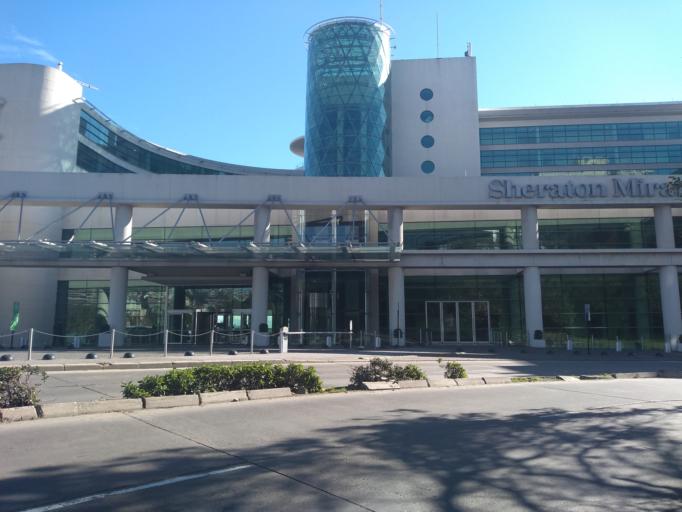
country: CL
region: Valparaiso
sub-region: Provincia de Valparaiso
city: Vina del Mar
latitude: -33.0216
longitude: -71.5677
